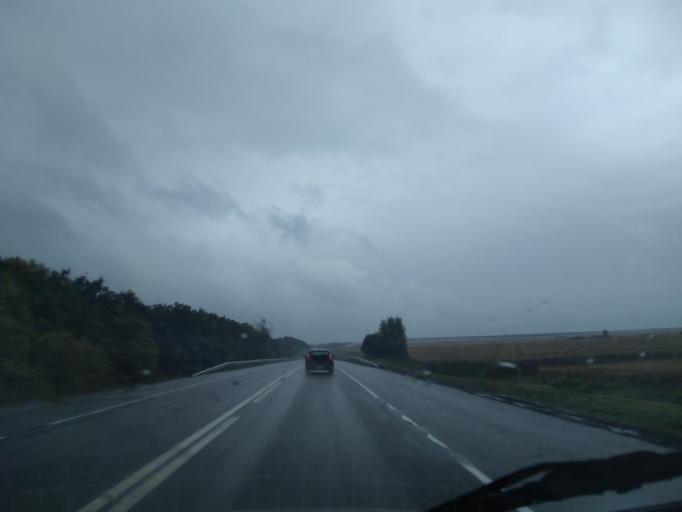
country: RU
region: Tula
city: Shchekino
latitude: 53.9706
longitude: 37.4782
